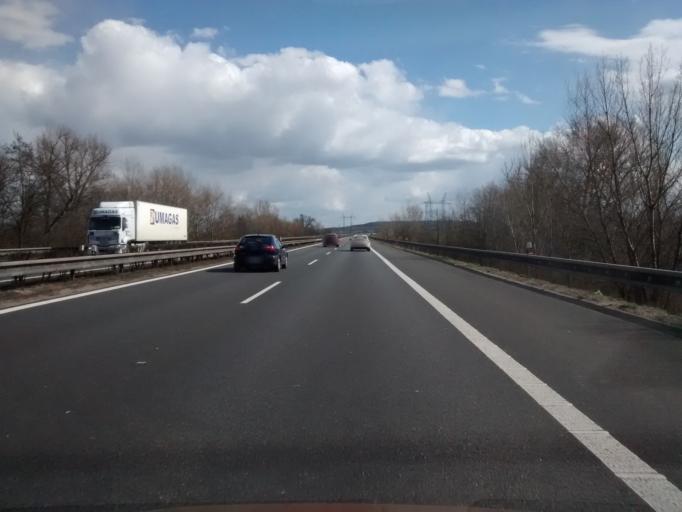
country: CZ
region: Central Bohemia
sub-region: Okres Melnik
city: Veltrusy
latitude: 50.3018
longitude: 14.3332
